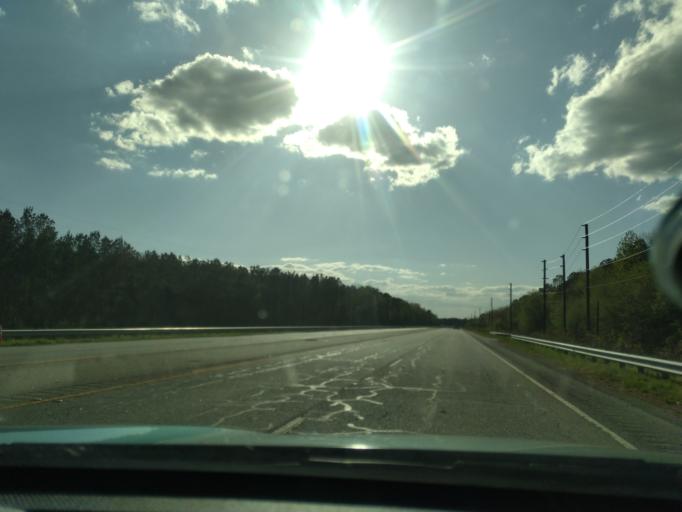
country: US
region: South Carolina
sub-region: Williamsburg County
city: Kingstree
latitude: 33.6578
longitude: -79.8602
